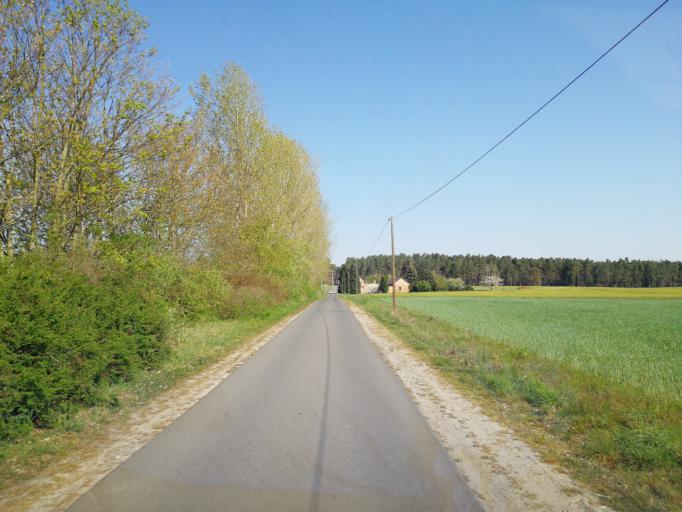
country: DE
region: Brandenburg
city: Sallgast
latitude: 51.6473
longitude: 13.8588
